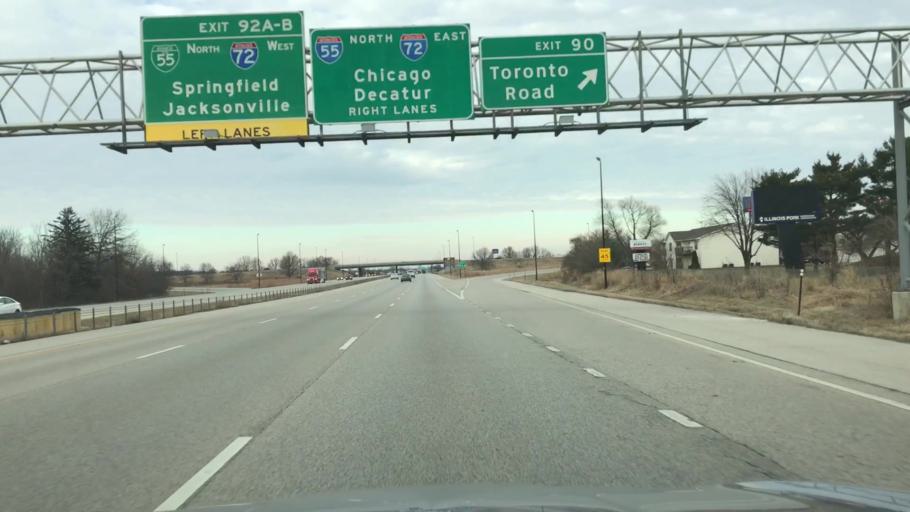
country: US
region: Illinois
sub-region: Sangamon County
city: Southern View
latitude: 39.7093
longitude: -89.6436
